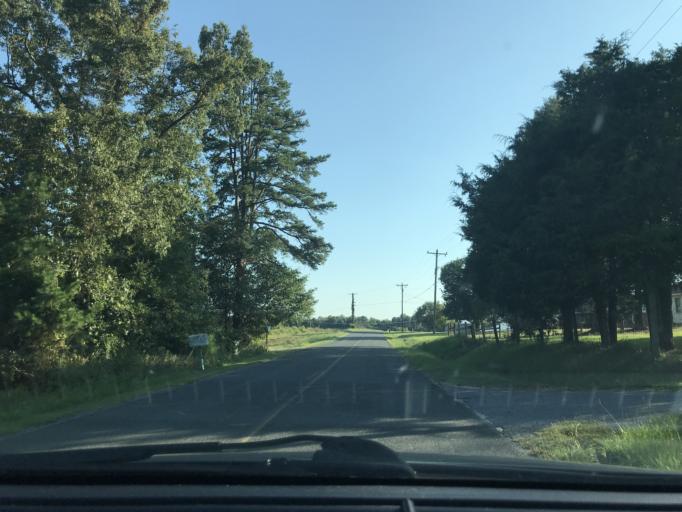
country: US
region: North Carolina
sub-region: Cleveland County
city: Boiling Springs
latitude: 35.1661
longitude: -81.7326
